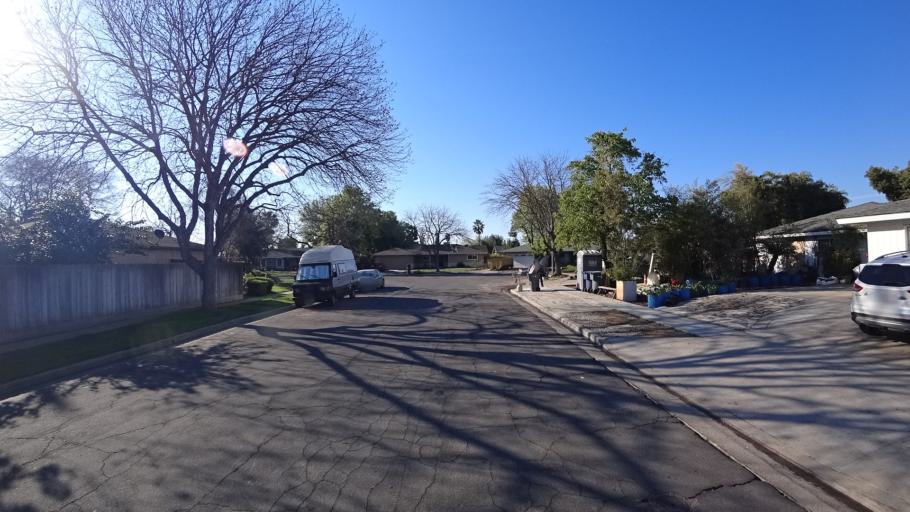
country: US
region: California
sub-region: Fresno County
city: Clovis
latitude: 36.8256
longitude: -119.7803
